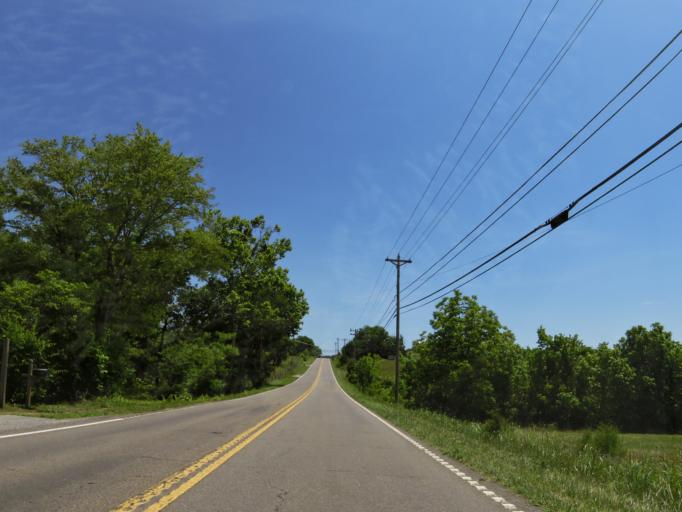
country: US
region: Tennessee
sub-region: Jefferson County
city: Dandridge
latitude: 36.0227
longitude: -83.4555
